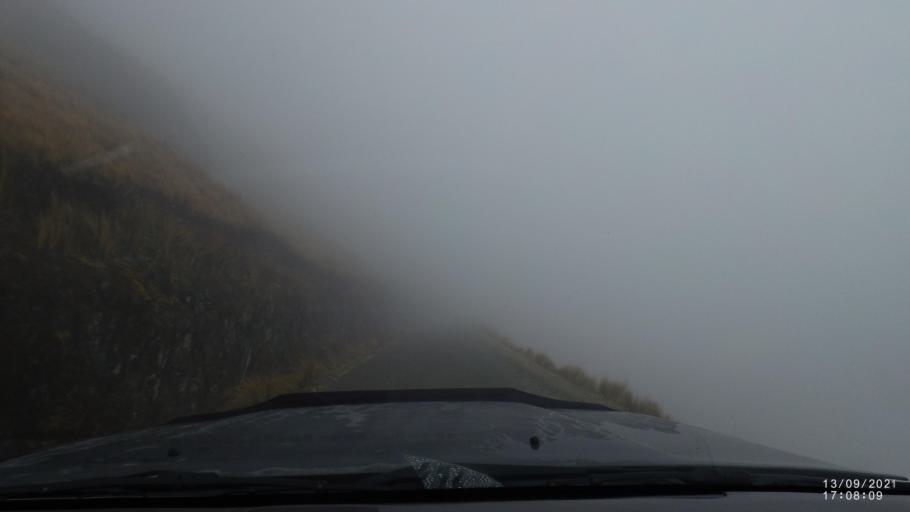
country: BO
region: Cochabamba
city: Colomi
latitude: -17.3291
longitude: -65.7293
